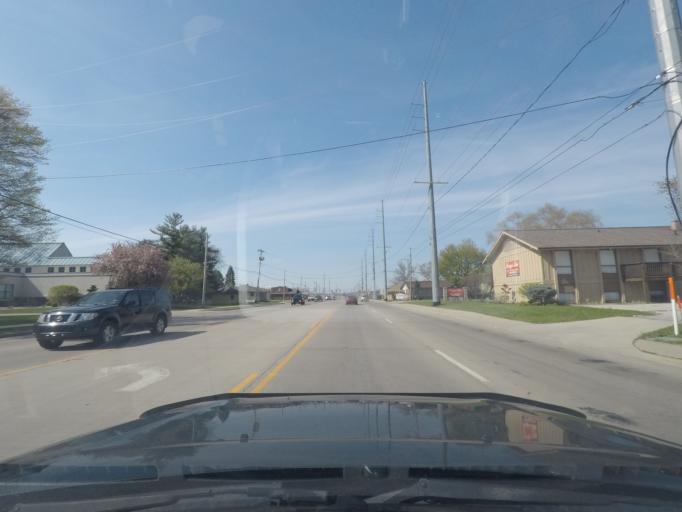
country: US
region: Indiana
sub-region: Elkhart County
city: Elkhart
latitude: 41.6861
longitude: -86.0034
